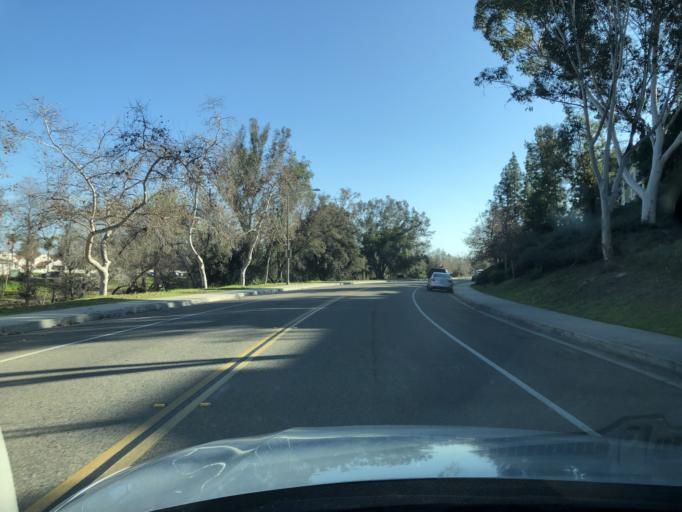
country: US
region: California
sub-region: San Diego County
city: Escondido
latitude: 33.1363
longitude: -117.0952
